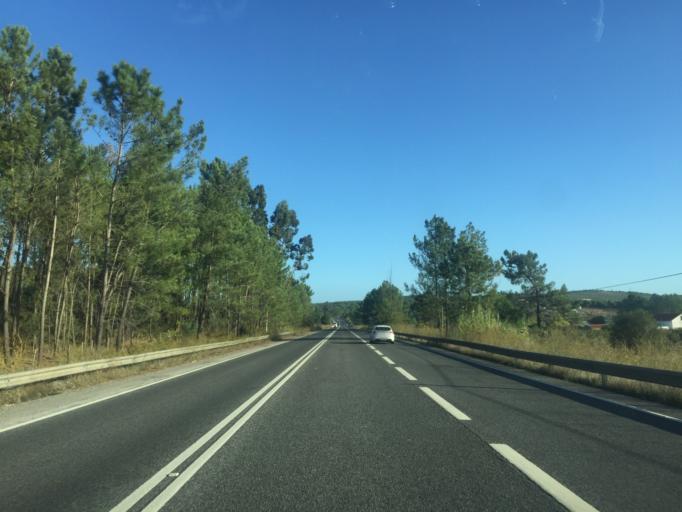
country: PT
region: Lisbon
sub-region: Azambuja
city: Alcoentre
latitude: 39.2432
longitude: -8.9556
